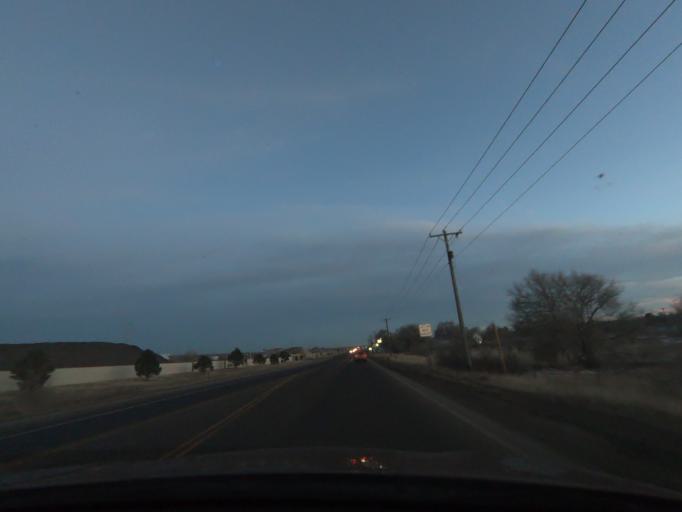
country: US
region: Colorado
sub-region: El Paso County
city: Stratmoor
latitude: 38.7752
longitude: -104.7686
